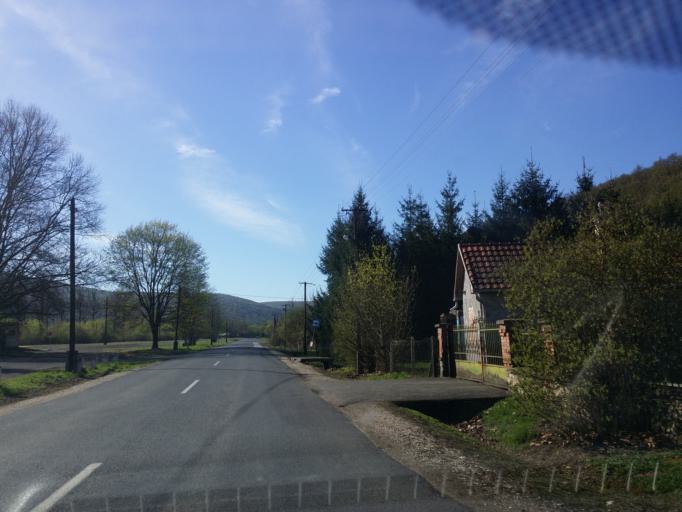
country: HU
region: Borsod-Abauj-Zemplen
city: Szendro
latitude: 48.4898
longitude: 20.6929
